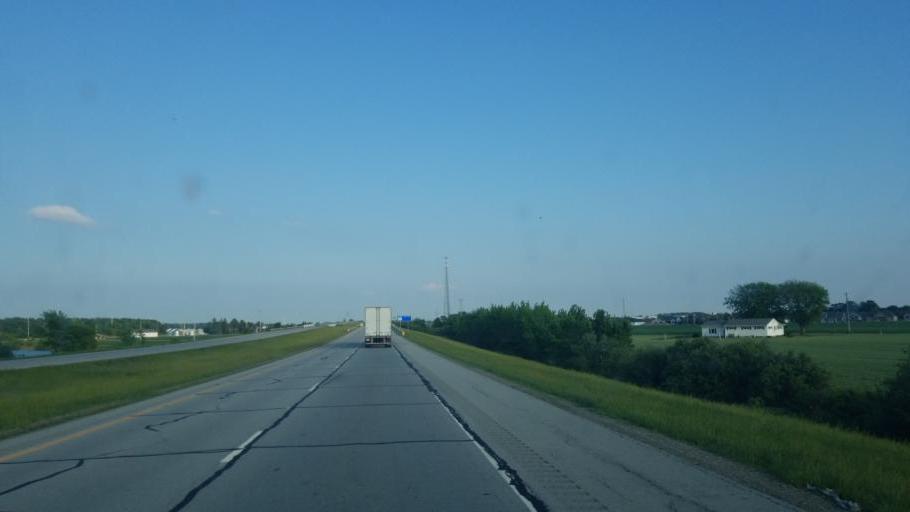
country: US
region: Ohio
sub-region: Allen County
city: Delphos
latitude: 40.8644
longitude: -84.3283
